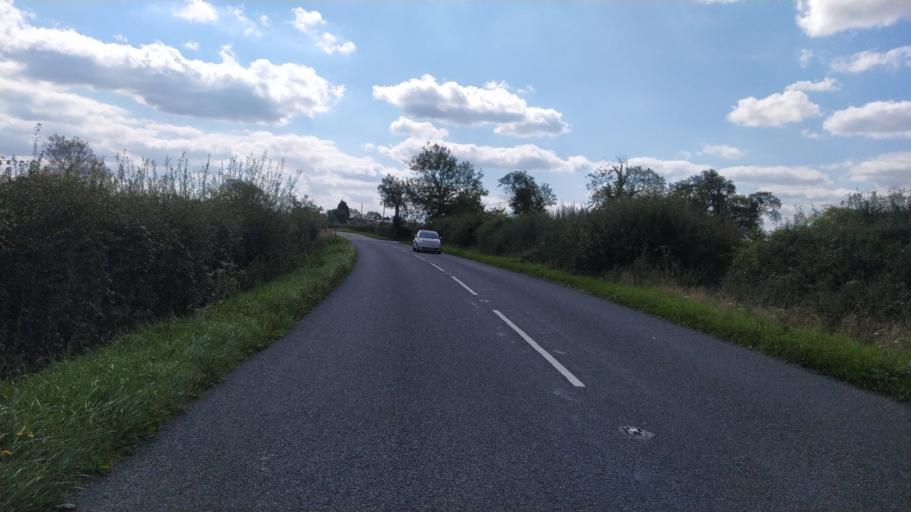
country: GB
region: England
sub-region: Wiltshire
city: Mere
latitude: 51.0807
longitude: -2.2808
